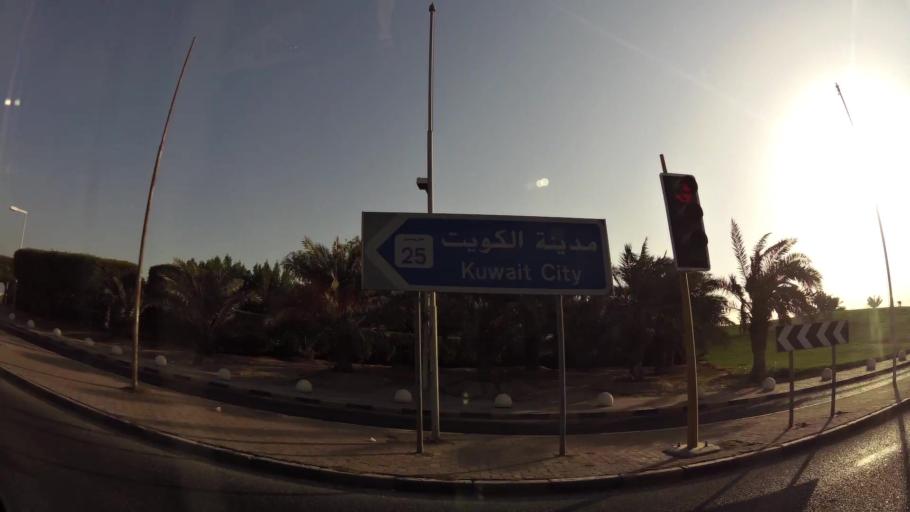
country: KW
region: Al Asimah
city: Ad Dasmah
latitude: 29.3600
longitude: 48.0250
